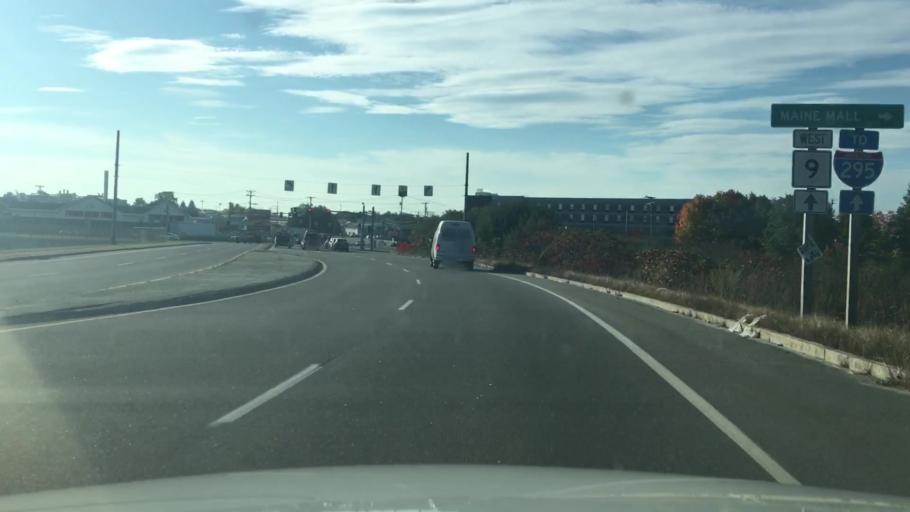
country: US
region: Maine
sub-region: Cumberland County
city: South Portland Gardens
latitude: 43.6457
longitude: -70.3307
